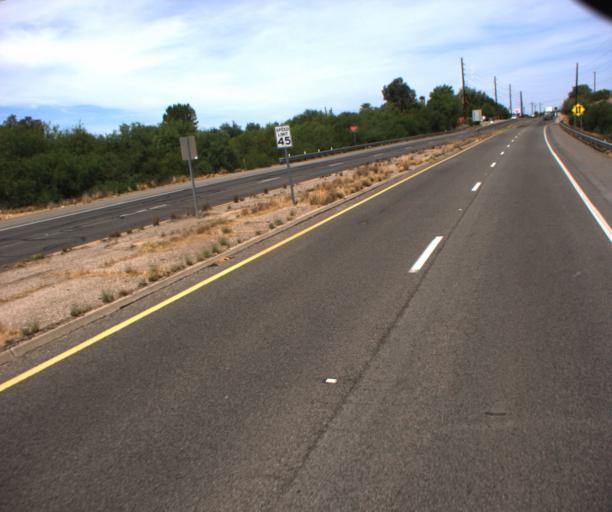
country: US
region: Arizona
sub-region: Maricopa County
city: Wickenburg
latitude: 33.9471
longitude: -112.7042
